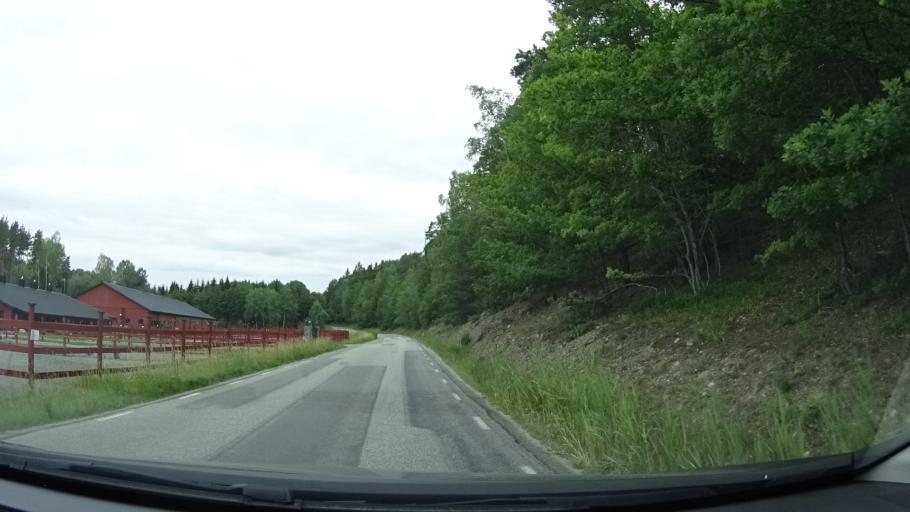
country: SE
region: Stockholm
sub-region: Varmdo Kommun
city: Hemmesta
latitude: 59.3610
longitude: 18.4823
